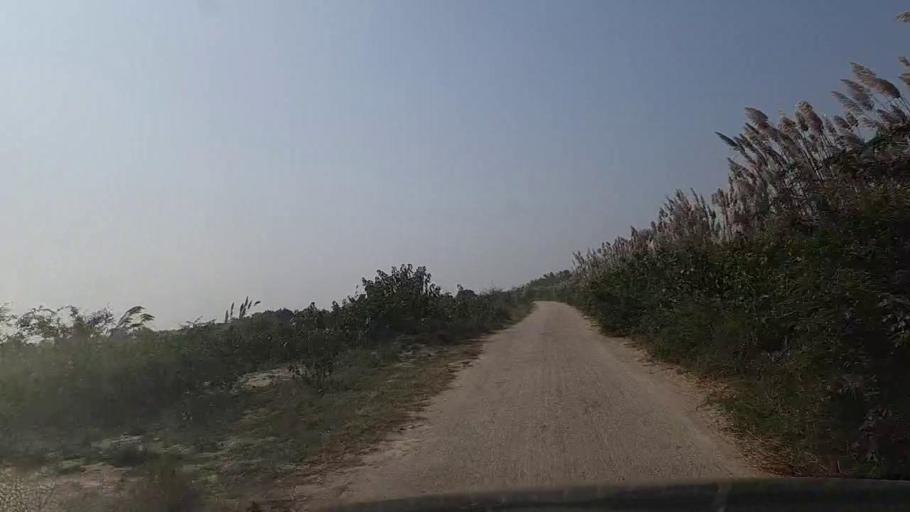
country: PK
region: Sindh
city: Gharo
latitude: 24.7081
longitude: 67.6496
